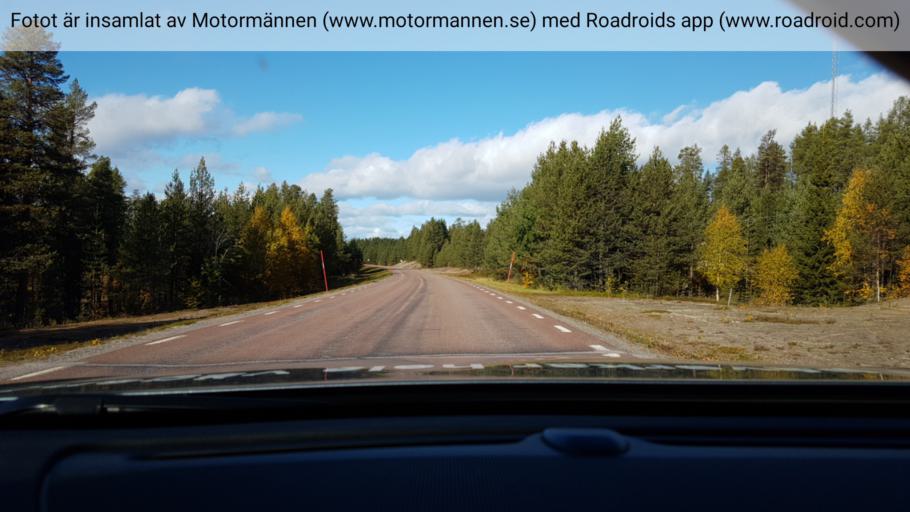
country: SE
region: Norrbotten
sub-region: Arjeplogs Kommun
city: Arjeplog
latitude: 66.0477
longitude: 18.0300
